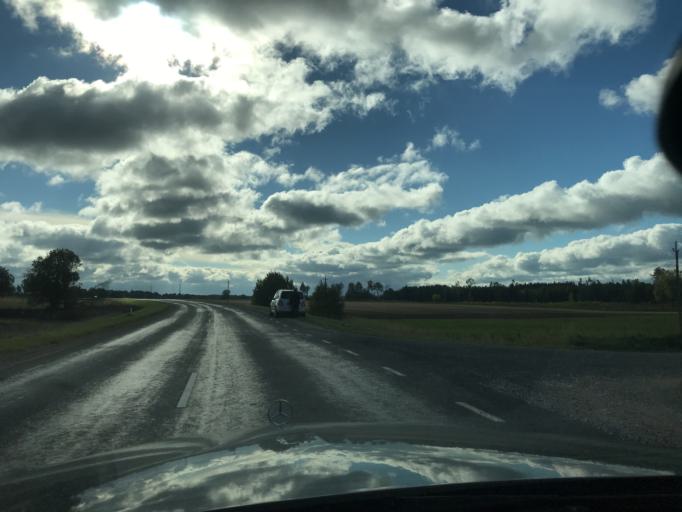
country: EE
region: Valgamaa
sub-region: Valga linn
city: Valga
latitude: 57.9723
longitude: 26.2607
